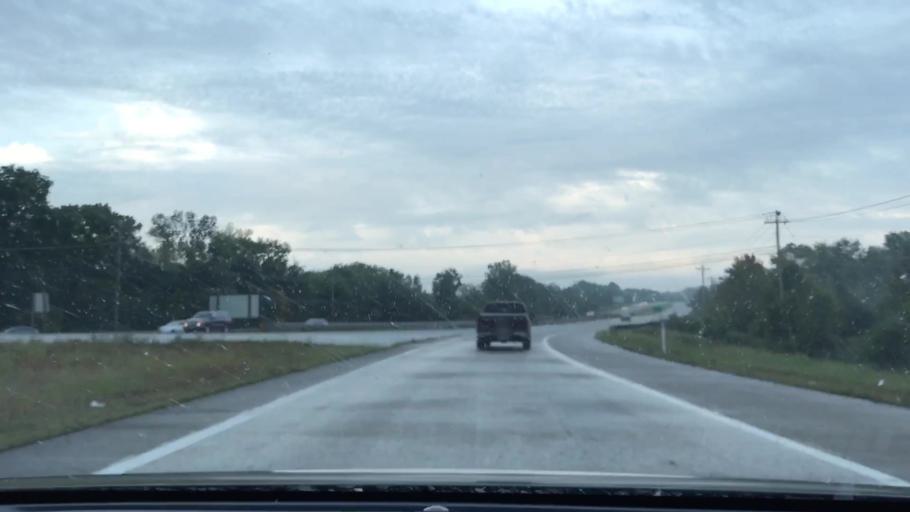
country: US
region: Tennessee
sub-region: Sumner County
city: Gallatin
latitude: 36.3892
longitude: -86.4757
